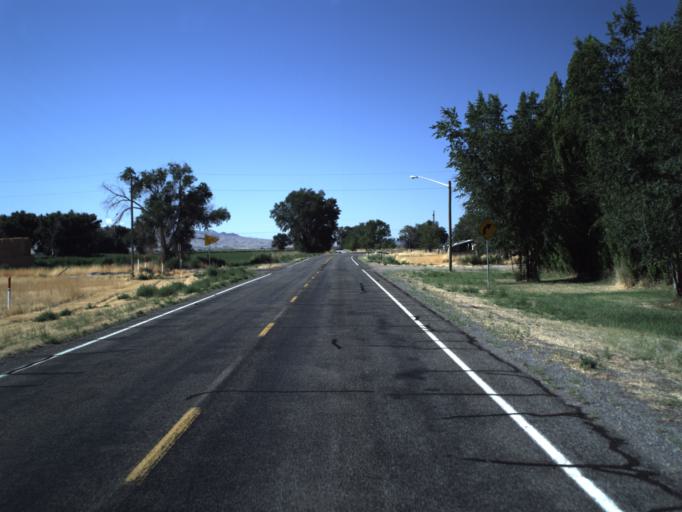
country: US
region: Utah
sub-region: Millard County
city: Delta
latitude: 39.5190
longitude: -112.3721
